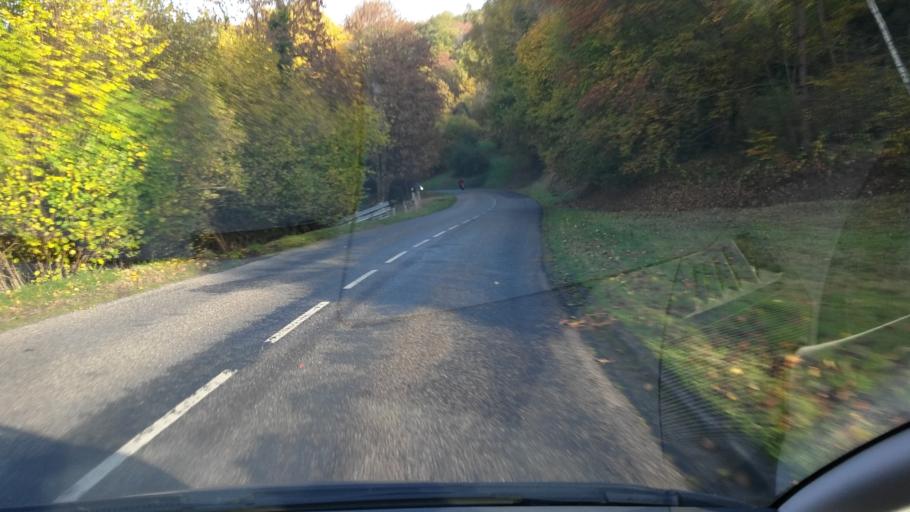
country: FR
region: Lorraine
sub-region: Departement de la Moselle
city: Dabo
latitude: 48.6911
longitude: 7.2069
